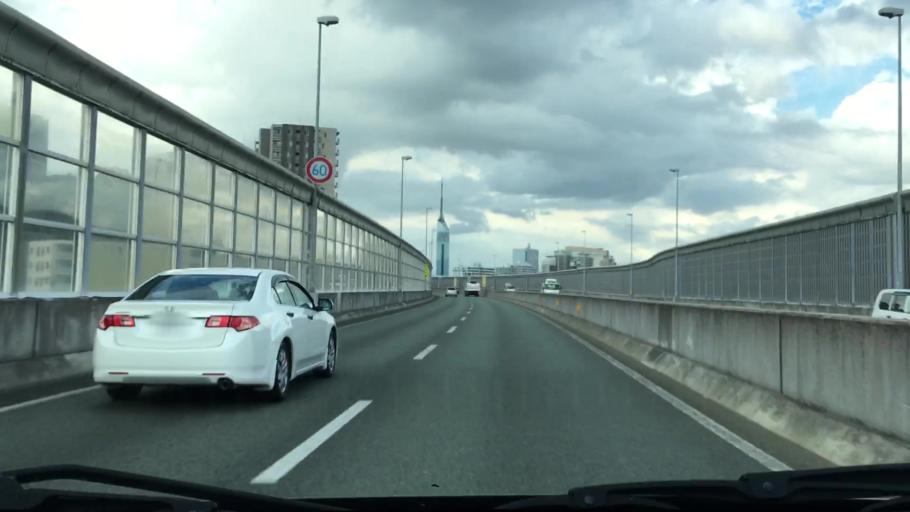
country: JP
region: Fukuoka
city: Fukuoka-shi
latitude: 33.5826
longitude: 130.3380
